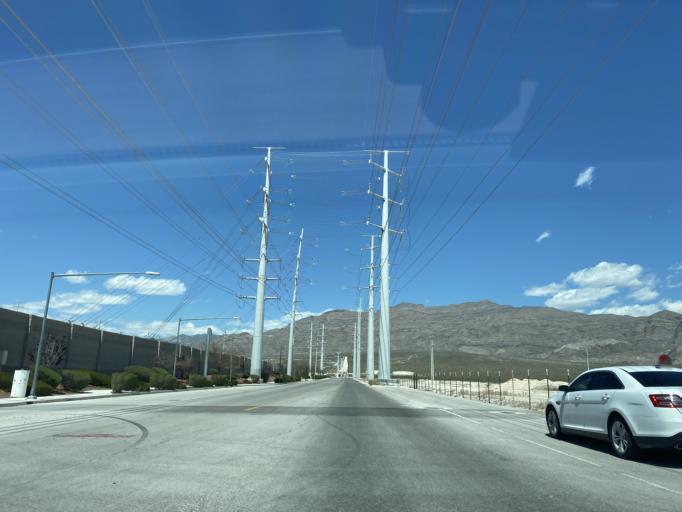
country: US
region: Nevada
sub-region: Clark County
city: North Las Vegas
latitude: 36.3207
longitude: -115.2071
